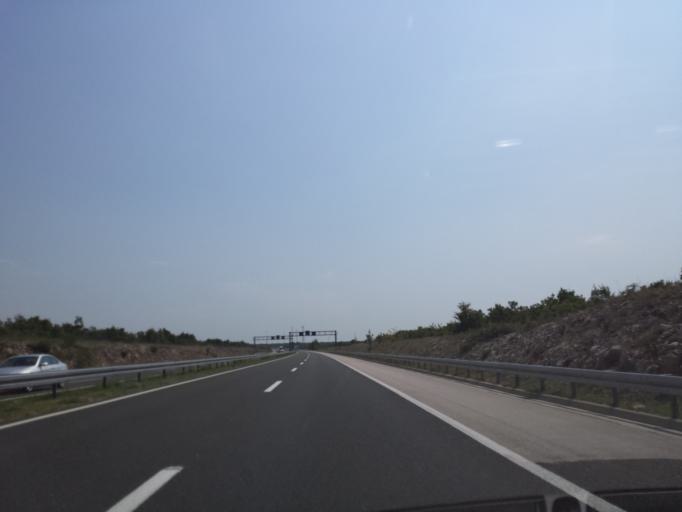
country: HR
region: Zadarska
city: Benkovac
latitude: 44.0184
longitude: 15.5755
